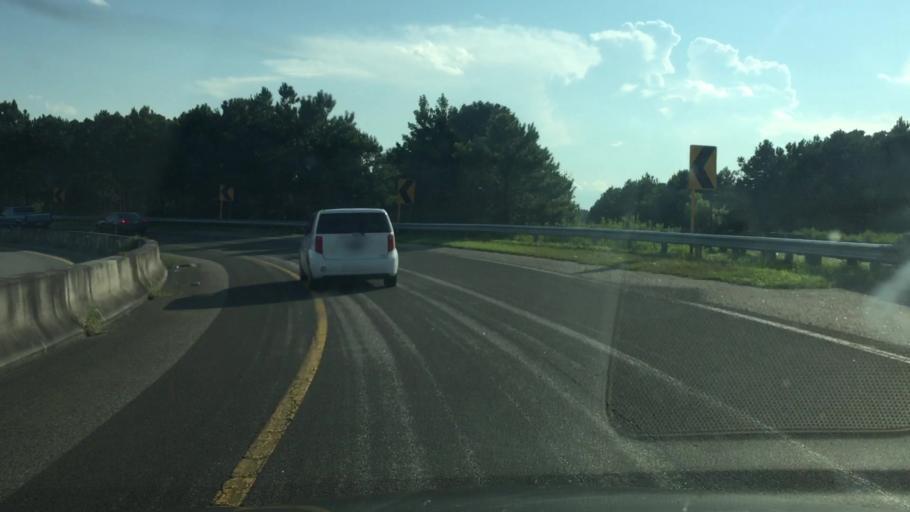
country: US
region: South Carolina
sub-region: Horry County
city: Forestbrook
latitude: 33.7409
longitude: -78.9535
